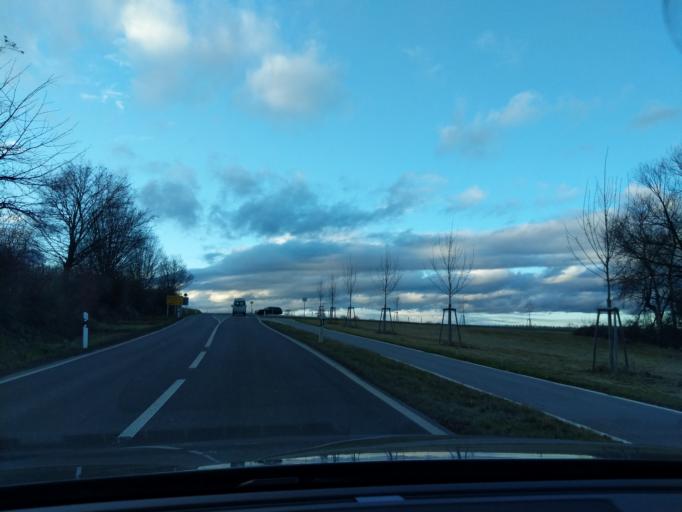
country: DE
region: Baden-Wuerttemberg
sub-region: Tuebingen Region
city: Bermatingen
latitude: 47.7285
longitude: 9.3156
